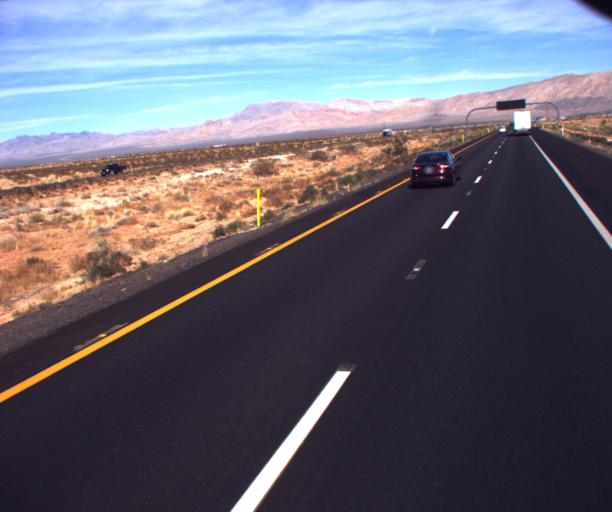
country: US
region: Arizona
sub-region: Mohave County
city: Beaver Dam
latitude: 36.8820
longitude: -113.9442
